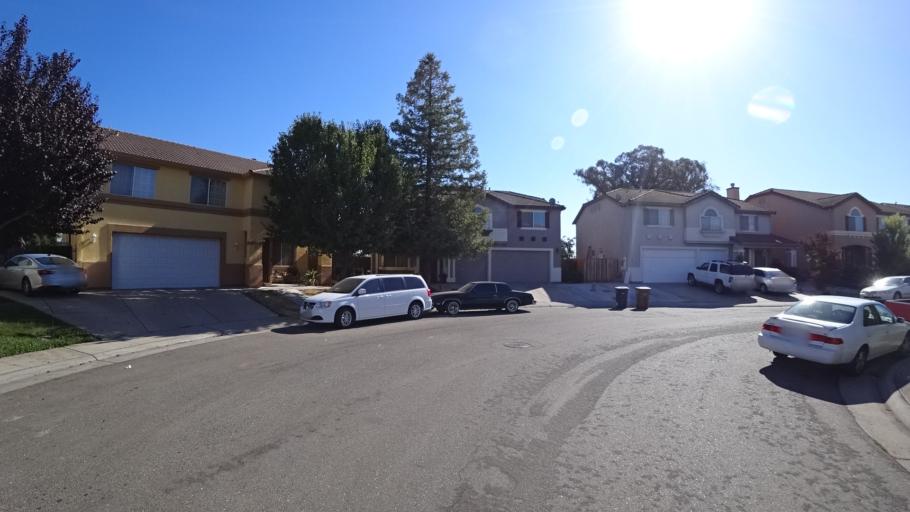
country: US
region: California
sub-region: Sacramento County
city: Laguna
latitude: 38.4408
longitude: -121.4368
